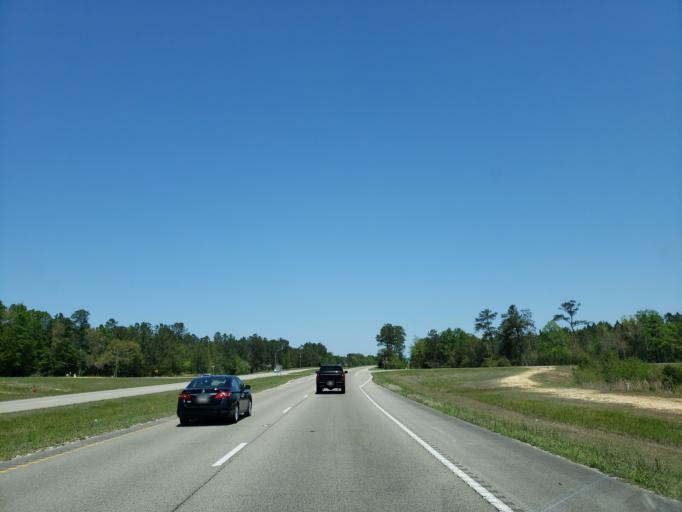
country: US
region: Mississippi
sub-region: Harrison County
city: Saucier
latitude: 30.6438
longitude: -89.1330
